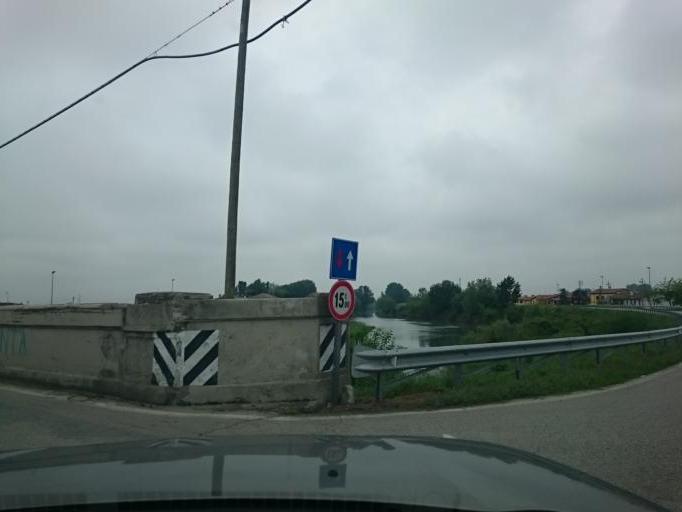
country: IT
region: Veneto
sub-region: Provincia di Padova
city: Codevigo
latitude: 45.2331
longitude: 12.1104
